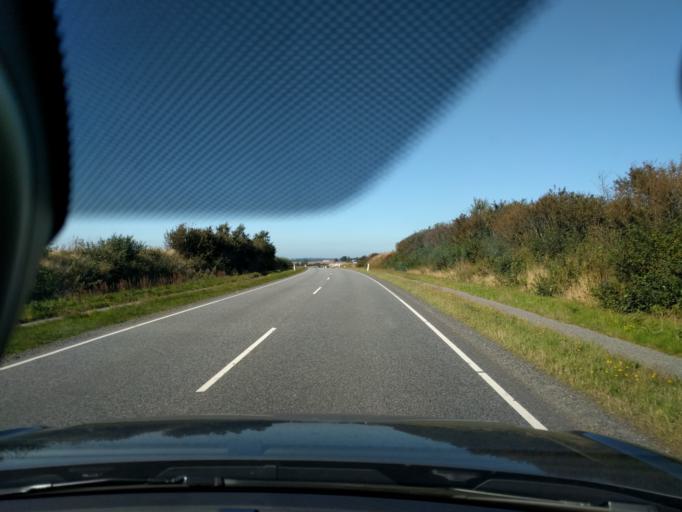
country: DK
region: North Denmark
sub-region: Vesthimmerland Kommune
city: Aars
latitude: 56.7399
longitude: 9.5986
